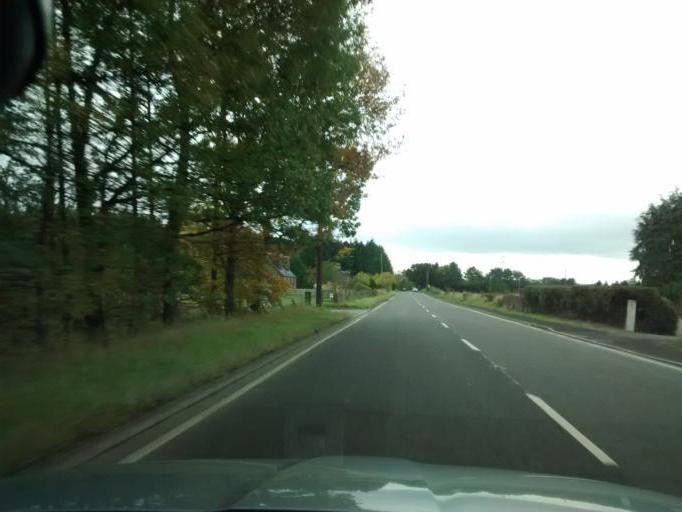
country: GB
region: Scotland
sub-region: Perth and Kinross
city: Blairgowrie
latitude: 56.5644
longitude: -3.3482
